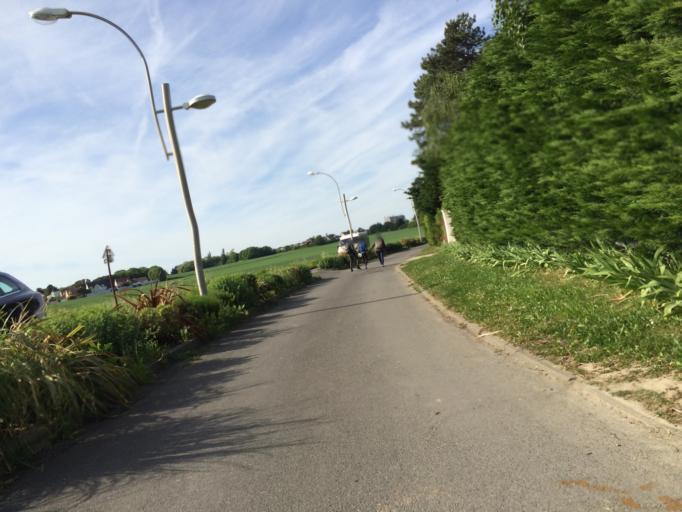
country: FR
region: Ile-de-France
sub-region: Departement de l'Essonne
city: Ballainvilliers
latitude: 48.6789
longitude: 2.2908
